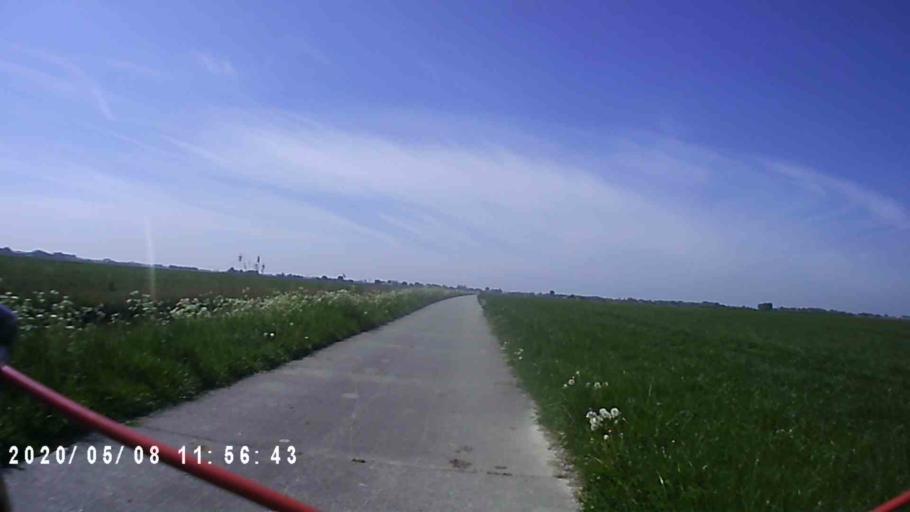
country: NL
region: Groningen
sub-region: Gemeente Bedum
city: Bedum
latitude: 53.3133
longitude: 6.6865
